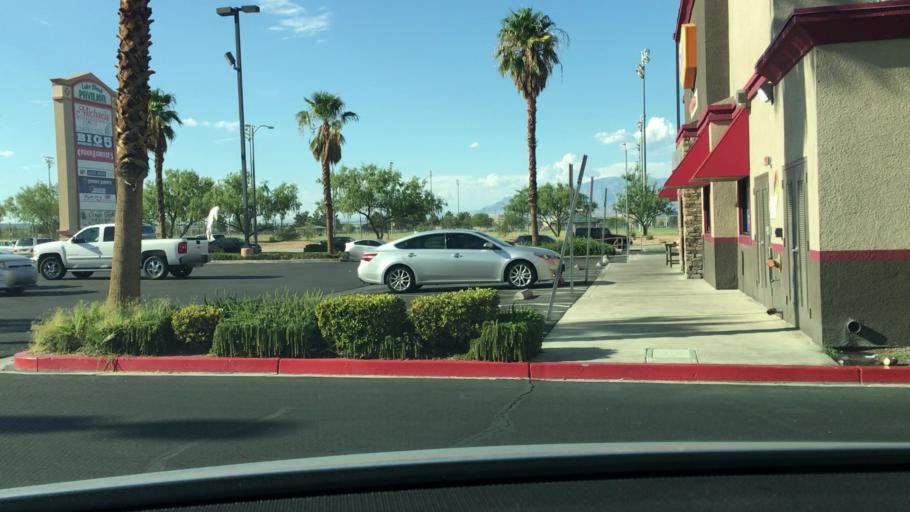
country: US
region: Nevada
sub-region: Clark County
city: Spring Valley
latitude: 36.1954
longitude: -115.2526
